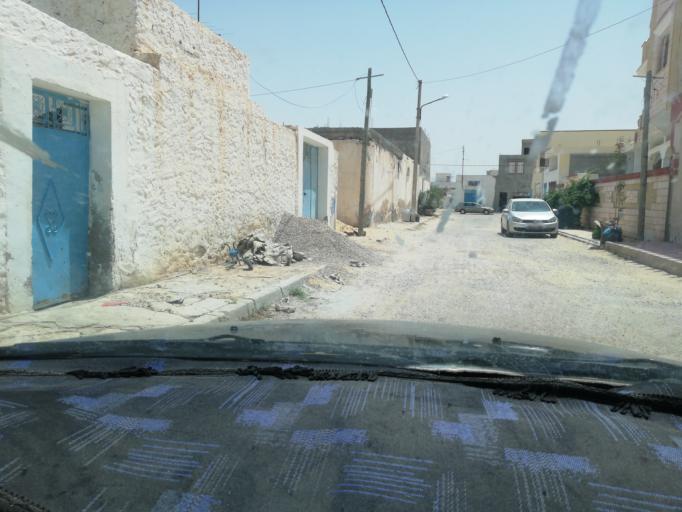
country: TN
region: Qabis
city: Matmata
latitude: 33.6183
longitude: 10.2842
